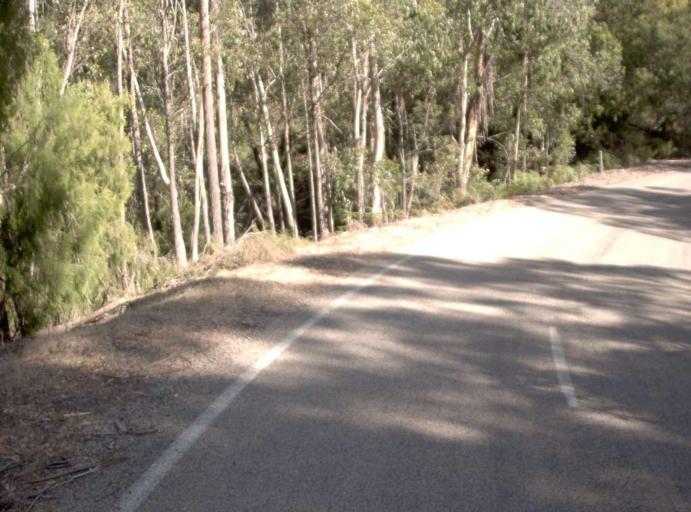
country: AU
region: Victoria
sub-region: East Gippsland
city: Lakes Entrance
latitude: -37.5665
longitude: 148.5475
